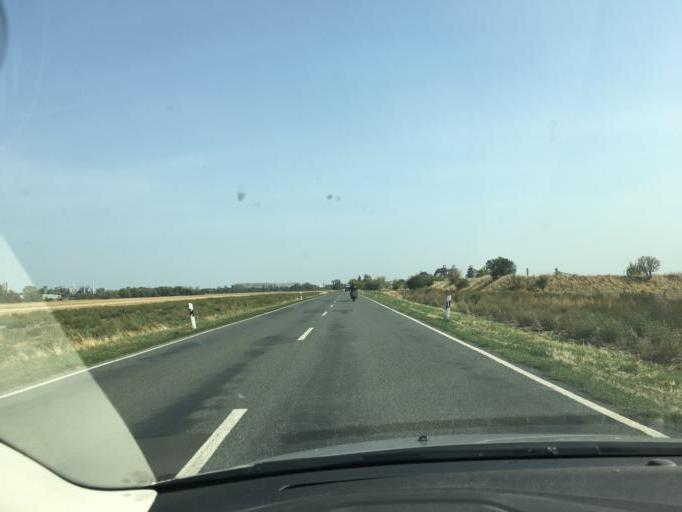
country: DE
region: Saxony-Anhalt
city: Barby
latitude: 51.9869
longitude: 11.8508
